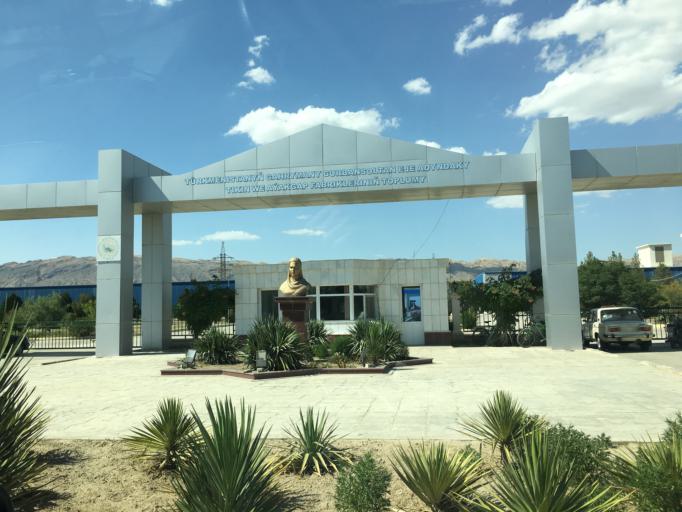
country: TM
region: Balkan
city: Magtymguly
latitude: 38.4403
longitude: 56.2645
